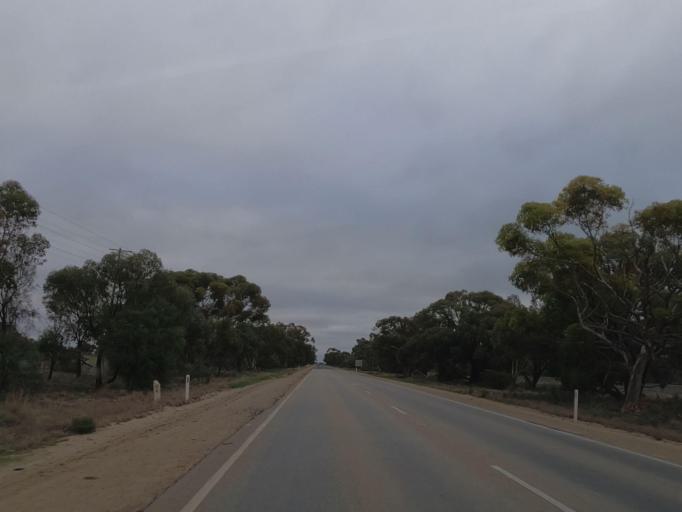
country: AU
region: Victoria
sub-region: Swan Hill
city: Swan Hill
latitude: -35.4025
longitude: 143.5785
